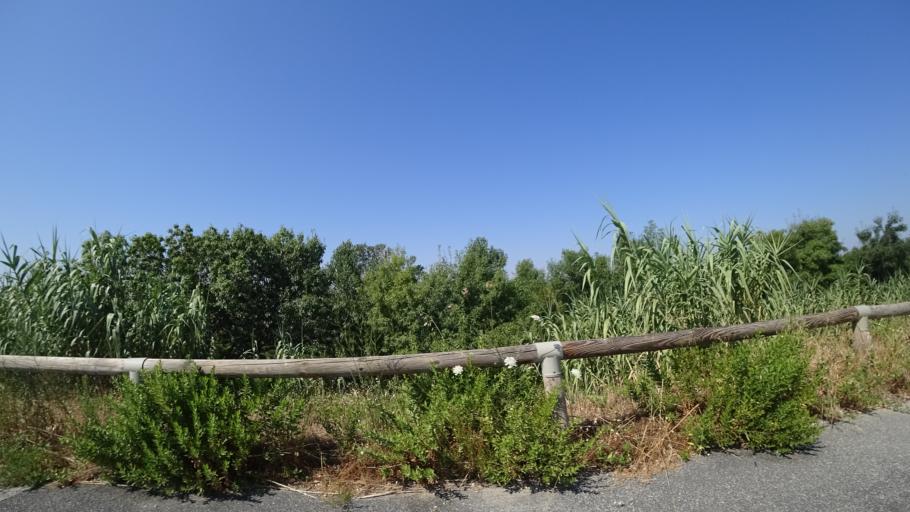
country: FR
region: Languedoc-Roussillon
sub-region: Departement des Pyrenees-Orientales
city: Claira
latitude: 42.7580
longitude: 2.9361
